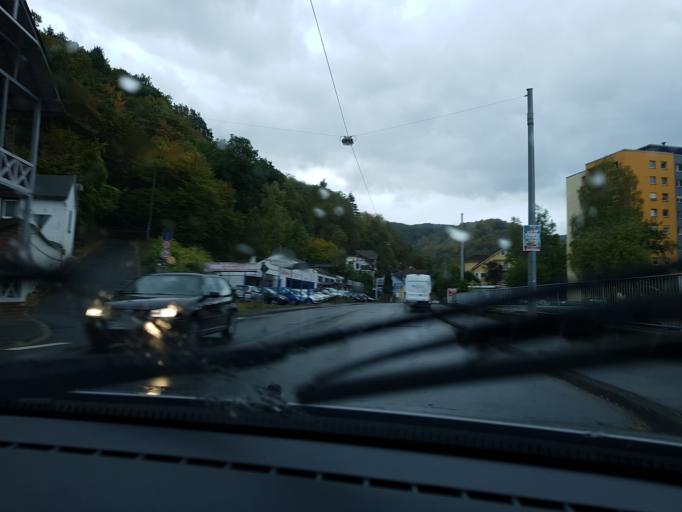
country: DE
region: Rheinland-Pfalz
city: Bad Ems
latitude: 50.3233
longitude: 7.7331
